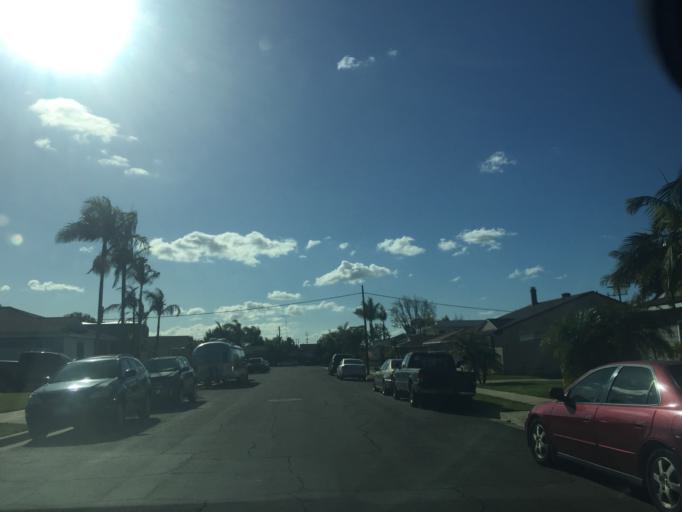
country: US
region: California
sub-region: San Diego County
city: La Mesa
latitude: 32.7909
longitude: -117.0791
